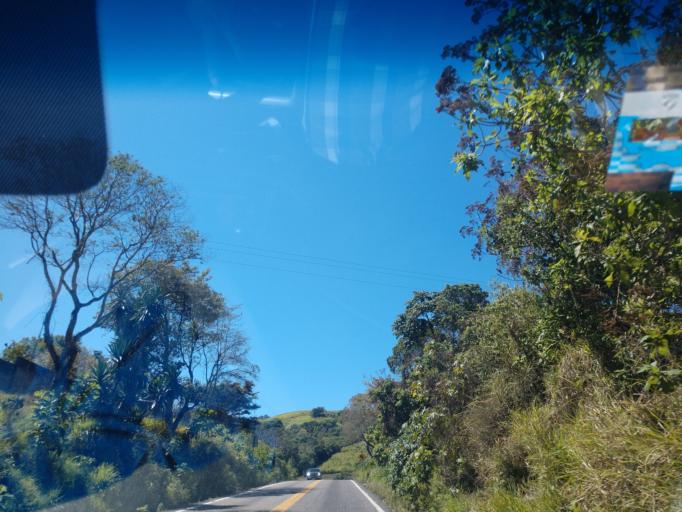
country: MX
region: Nayarit
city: Xalisco
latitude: 21.3647
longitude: -104.9178
